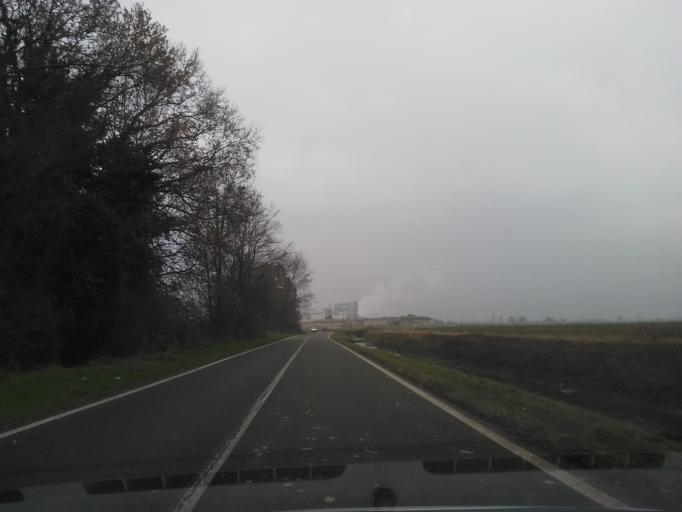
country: IT
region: Piedmont
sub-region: Provincia di Vercelli
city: Crova
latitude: 45.3242
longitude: 8.2182
